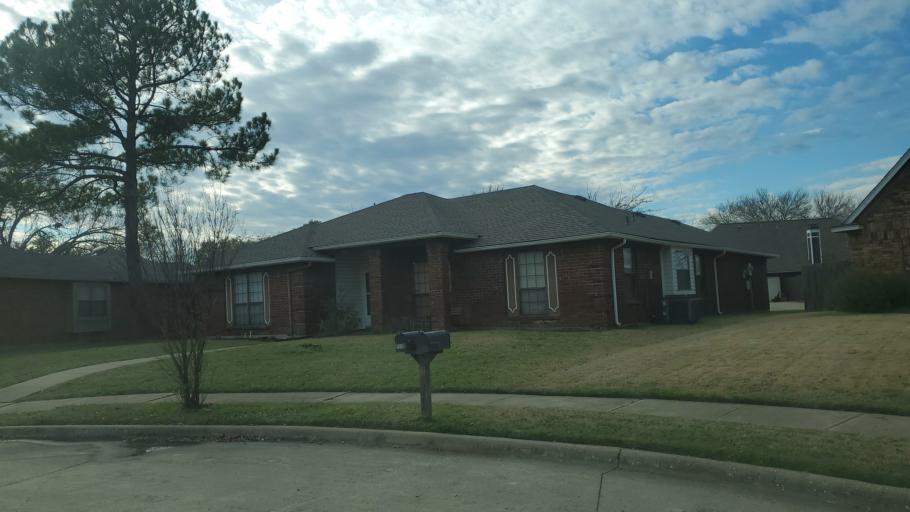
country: US
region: Texas
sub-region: Dallas County
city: Carrollton
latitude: 32.9946
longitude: -96.8986
